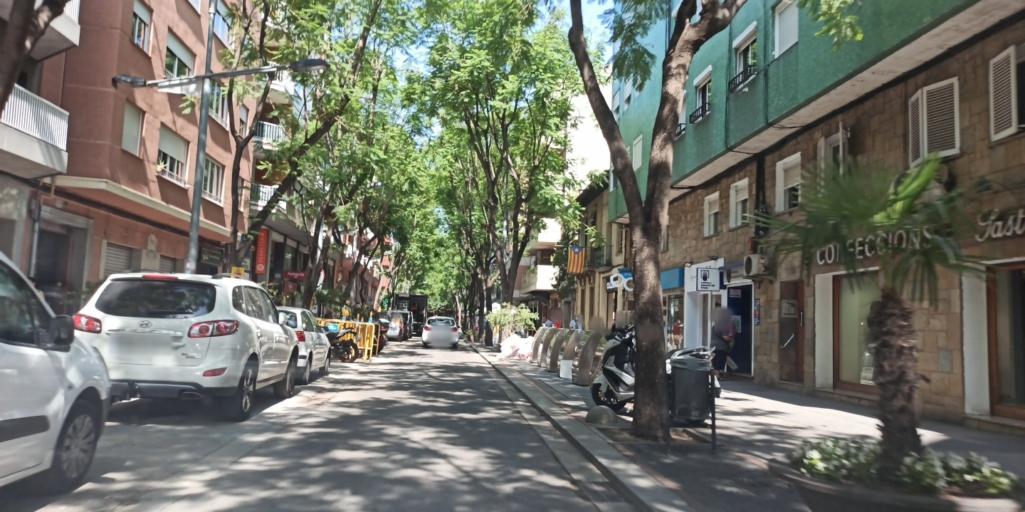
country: ES
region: Catalonia
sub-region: Provincia de Barcelona
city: Cerdanyola del Valles
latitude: 41.4929
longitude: 2.1452
